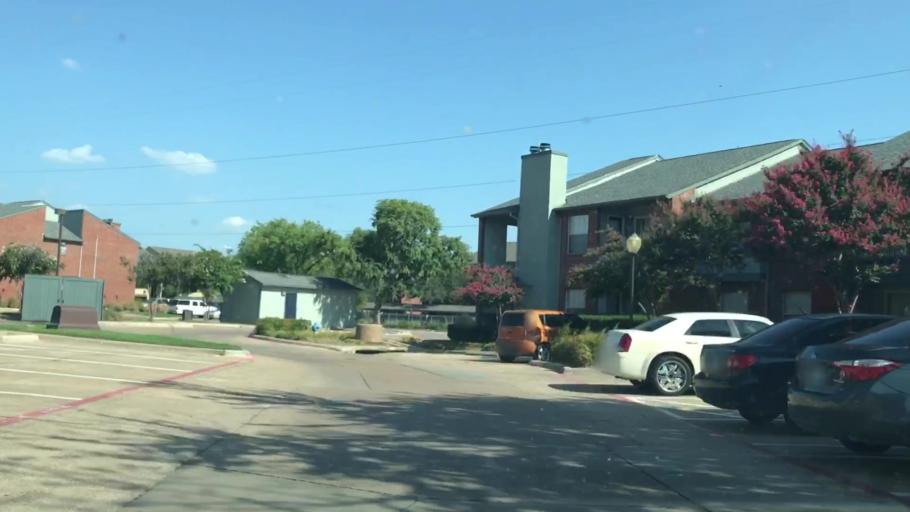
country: US
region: Texas
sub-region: Dallas County
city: Mesquite
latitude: 32.8184
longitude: -96.6349
